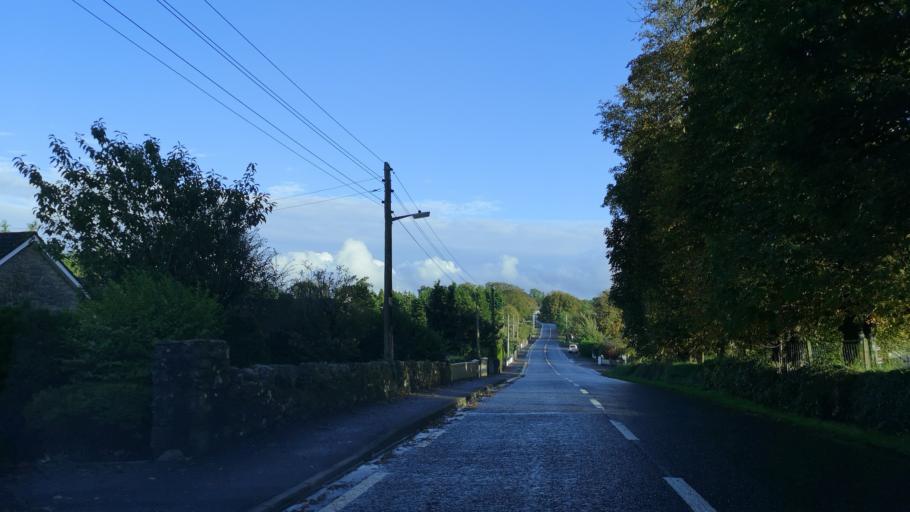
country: IE
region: Connaught
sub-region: Roscommon
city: Castlerea
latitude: 53.7614
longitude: -8.4727
